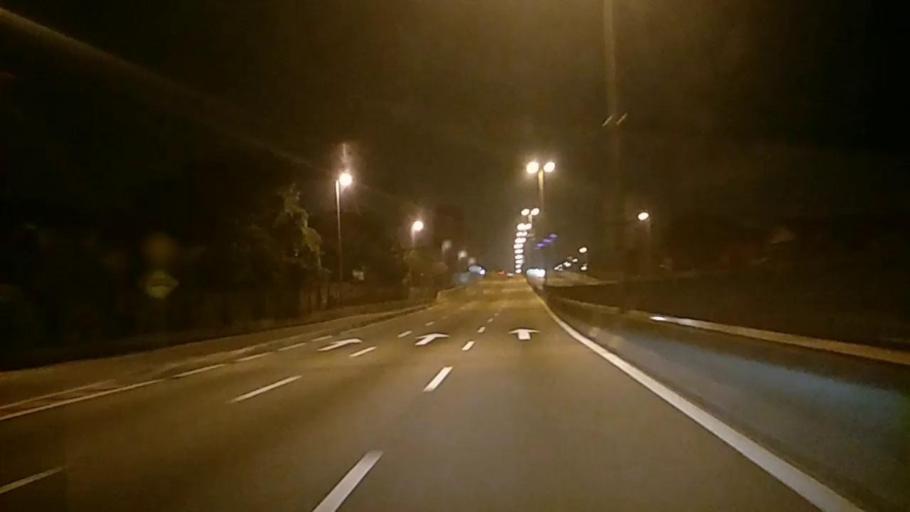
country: MY
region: Selangor
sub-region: Petaling
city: Petaling Jaya
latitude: 3.0712
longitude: 101.6136
